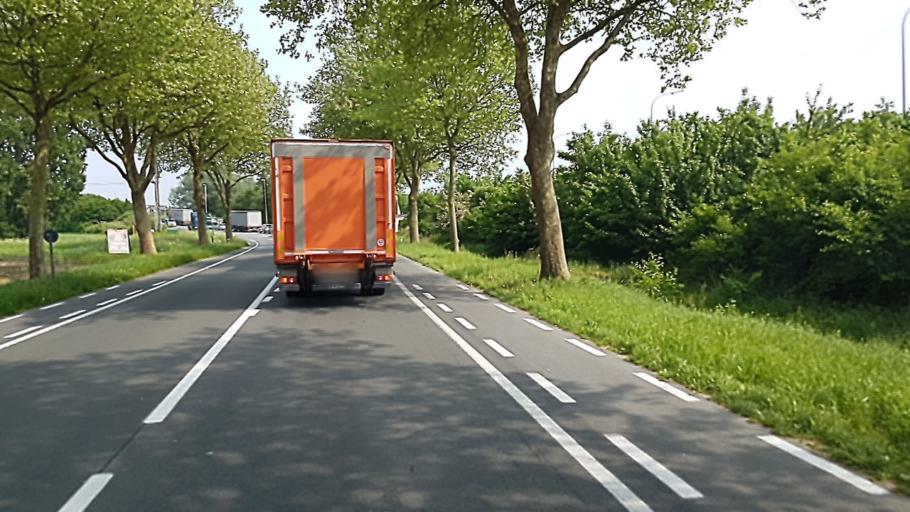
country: BE
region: Flanders
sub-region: Provincie West-Vlaanderen
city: Wevelgem
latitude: 50.8311
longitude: 3.1925
